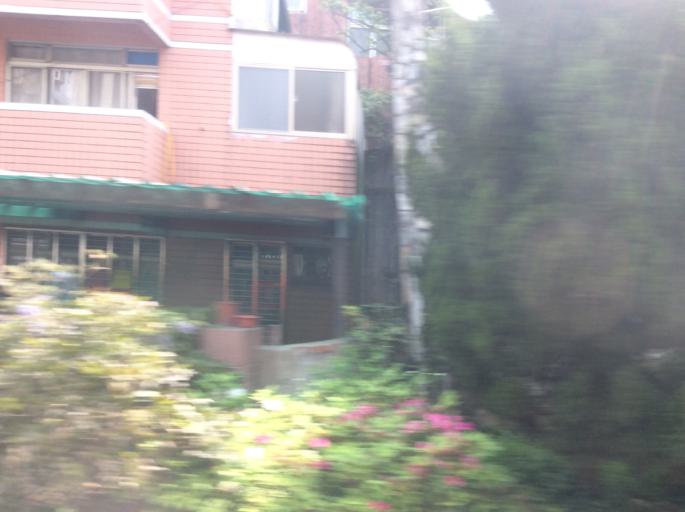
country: TW
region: Taipei
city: Taipei
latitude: 25.1418
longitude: 121.5497
